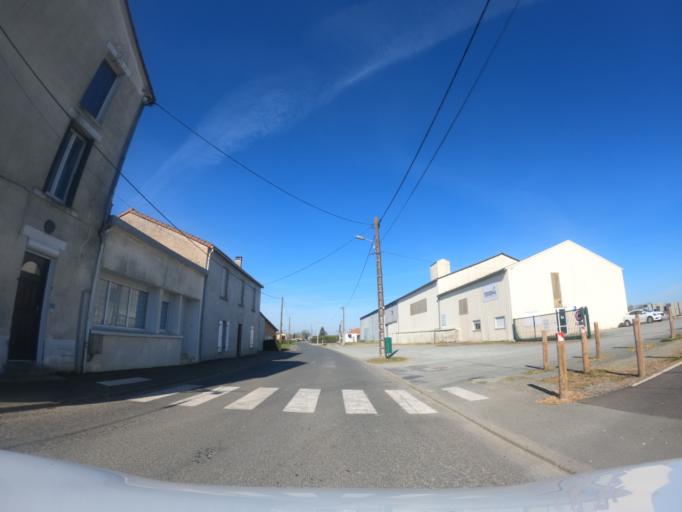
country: FR
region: Pays de la Loire
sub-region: Departement de la Vendee
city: Saint-Pierre-du-Chemin
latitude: 46.6965
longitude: -0.7046
